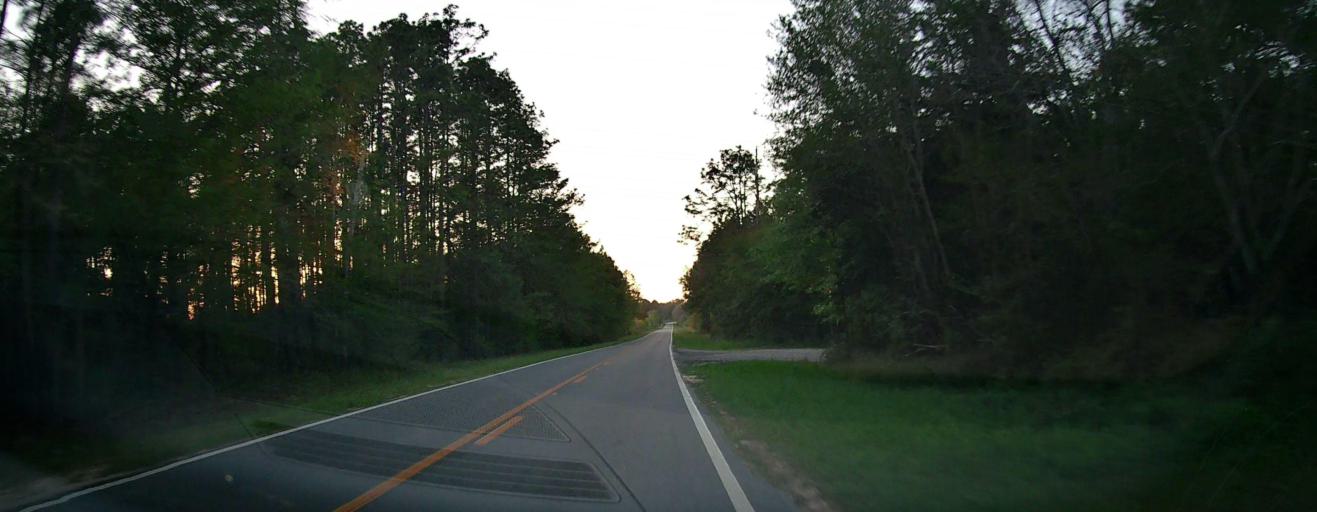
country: US
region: Georgia
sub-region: Wilcox County
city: Rochelle
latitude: 31.7953
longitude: -83.4445
